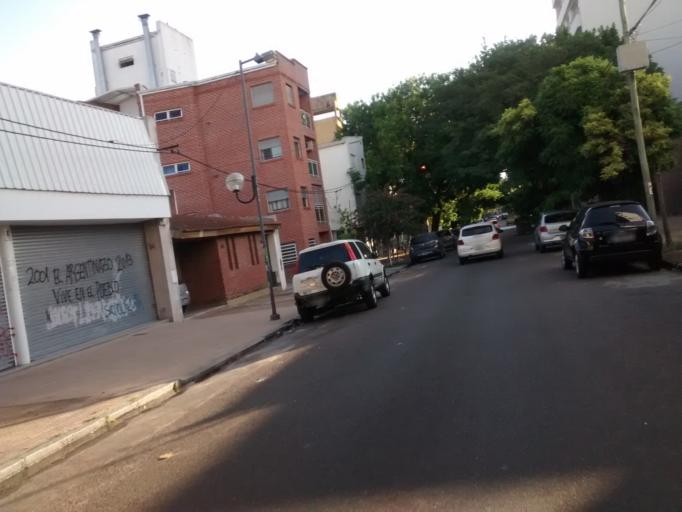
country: AR
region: Buenos Aires
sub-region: Partido de La Plata
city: La Plata
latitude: -34.9254
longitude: -57.9383
